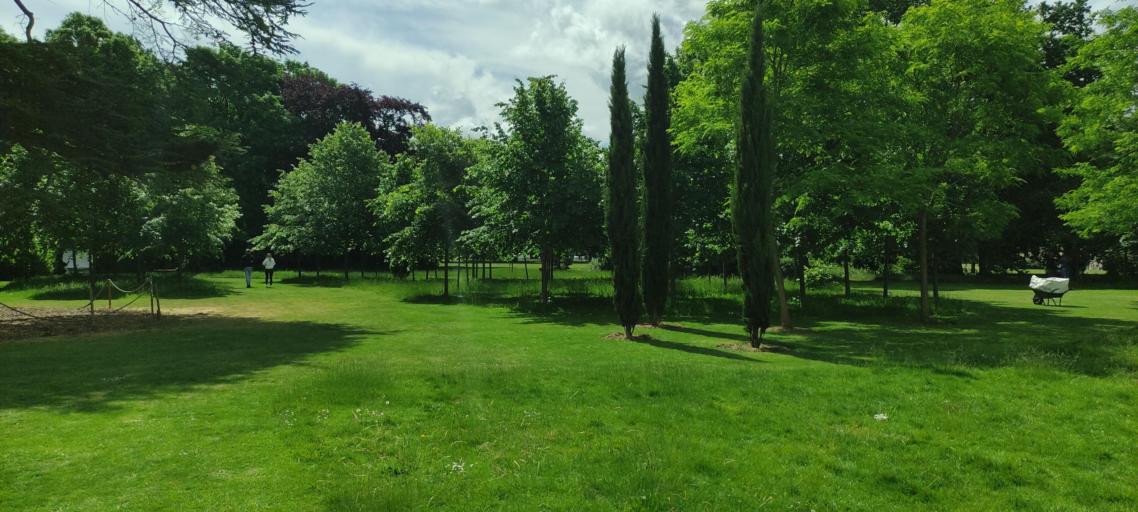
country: GB
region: England
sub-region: Greater London
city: Twickenham
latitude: 51.4381
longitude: -0.3343
